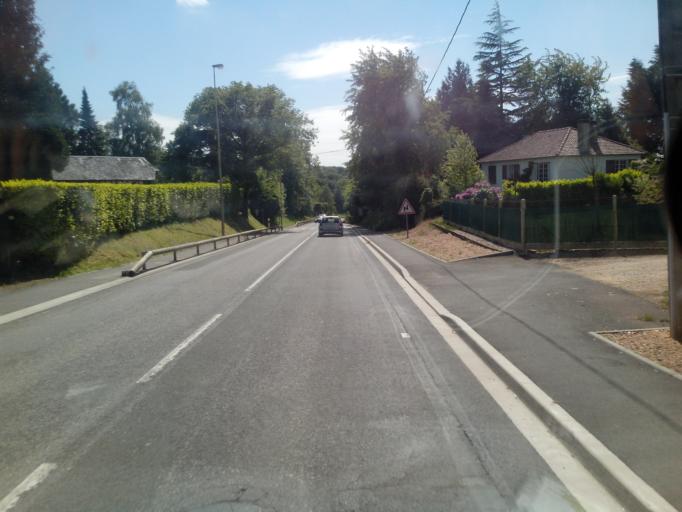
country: FR
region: Haute-Normandie
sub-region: Departement de l'Eure
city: Beuzeville
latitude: 49.3428
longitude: 0.3355
